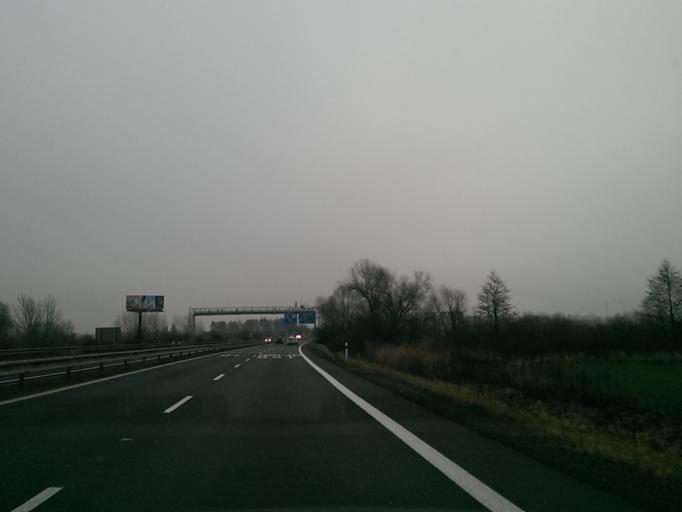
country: CZ
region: Olomoucky
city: Horka nad Moravou
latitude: 49.6061
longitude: 17.2144
